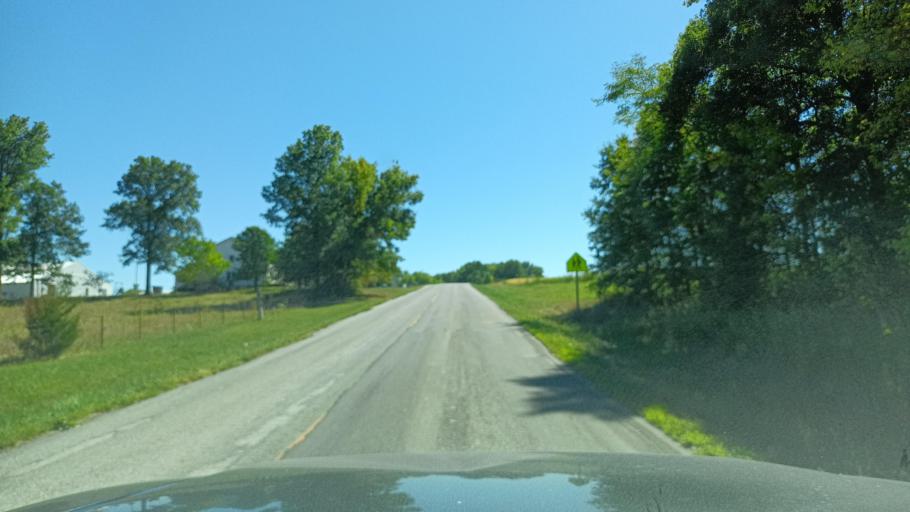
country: US
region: Missouri
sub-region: Macon County
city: La Plata
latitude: 40.0207
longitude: -92.6000
